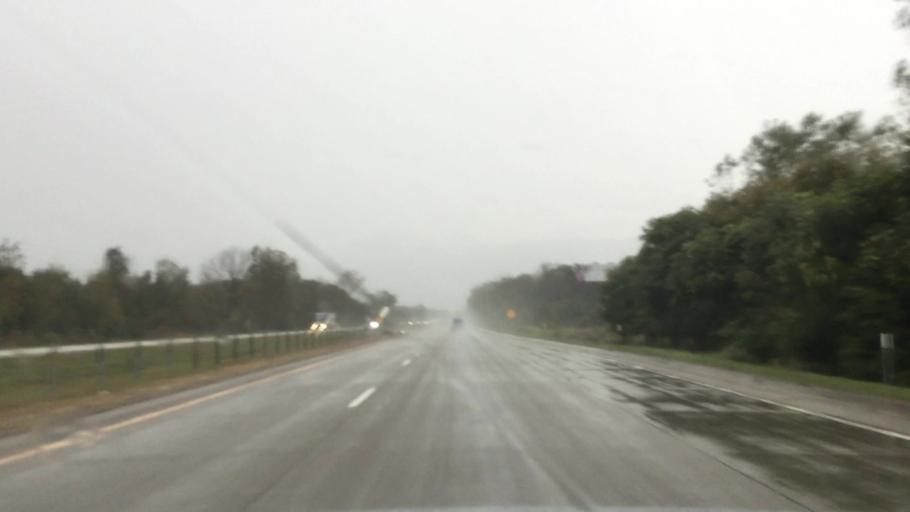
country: US
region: Michigan
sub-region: Van Buren County
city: Paw Paw
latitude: 42.2061
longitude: -85.8969
